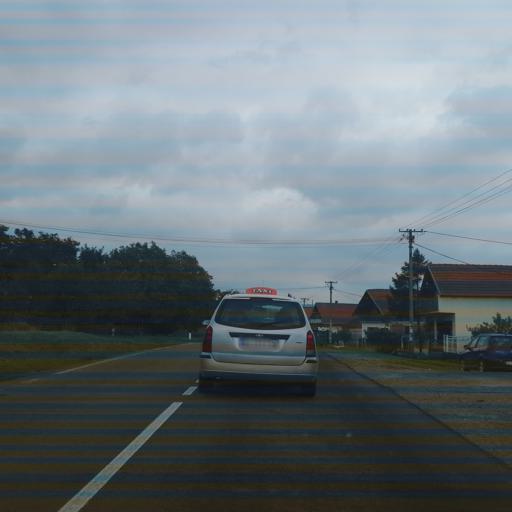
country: RS
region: Central Serbia
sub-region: Nisavski Okrug
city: Aleksinac
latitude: 43.5761
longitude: 21.6664
